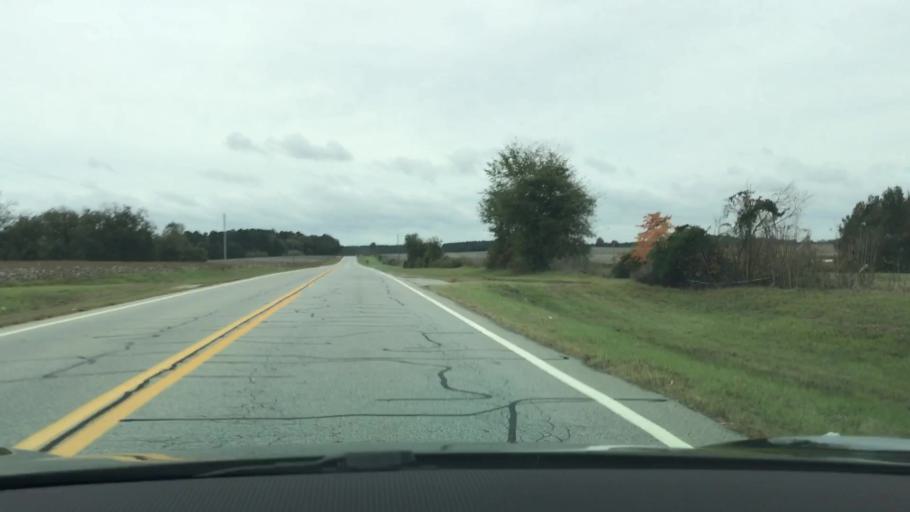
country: US
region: Georgia
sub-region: Warren County
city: Warrenton
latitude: 33.3671
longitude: -82.5997
